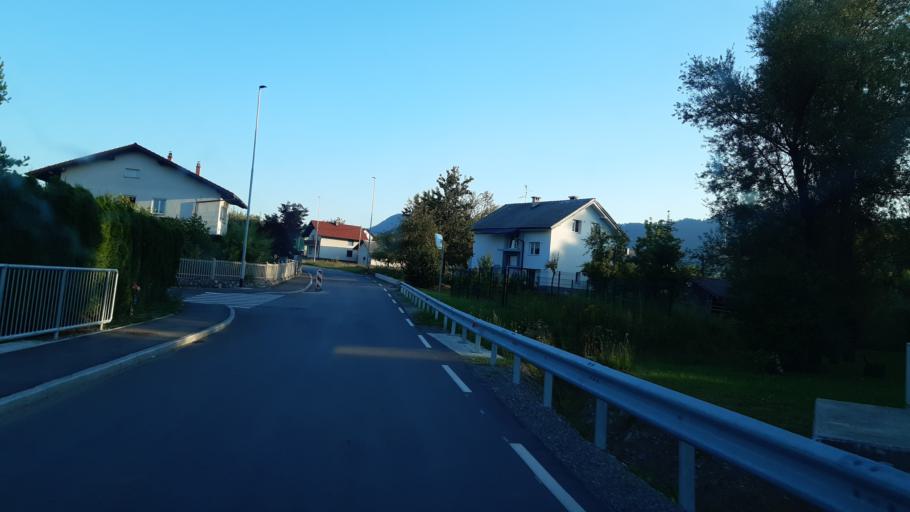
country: SI
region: Kocevje
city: Kocevje
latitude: 45.6501
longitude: 14.8797
